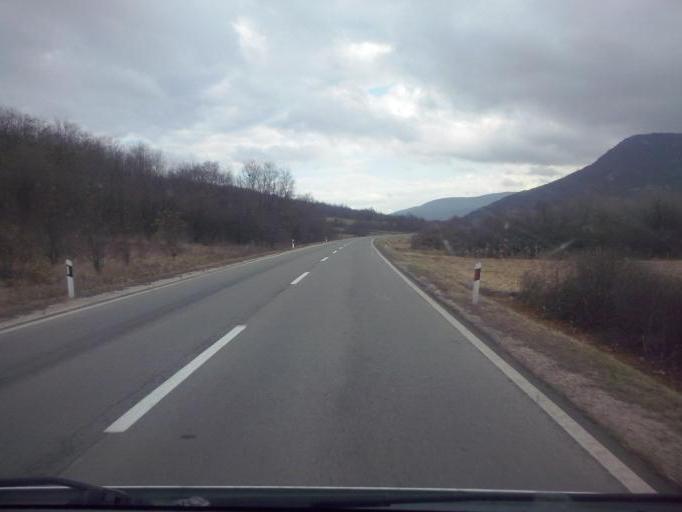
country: RS
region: Central Serbia
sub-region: Pomoravski Okrug
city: Paracin
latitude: 43.8633
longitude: 21.5081
